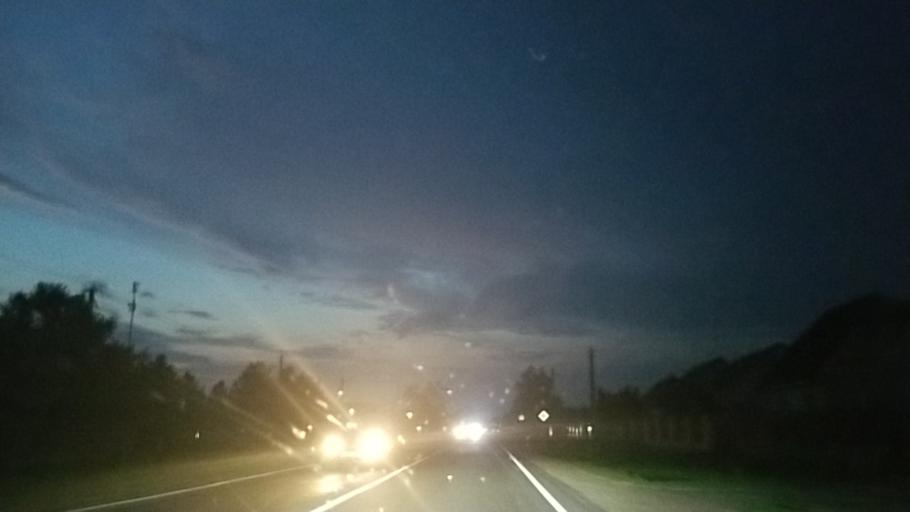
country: PL
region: Lublin Voivodeship
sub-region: Powiat bialski
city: Koden
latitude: 51.9251
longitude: 23.6608
